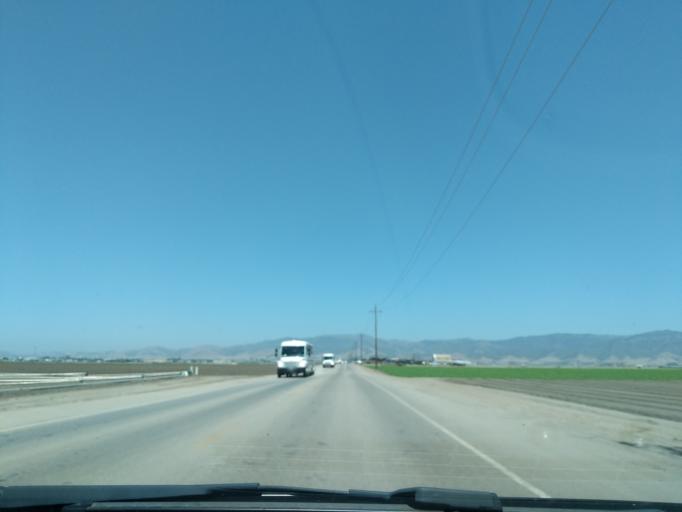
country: US
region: California
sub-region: Monterey County
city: Salinas
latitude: 36.6284
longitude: -121.6266
